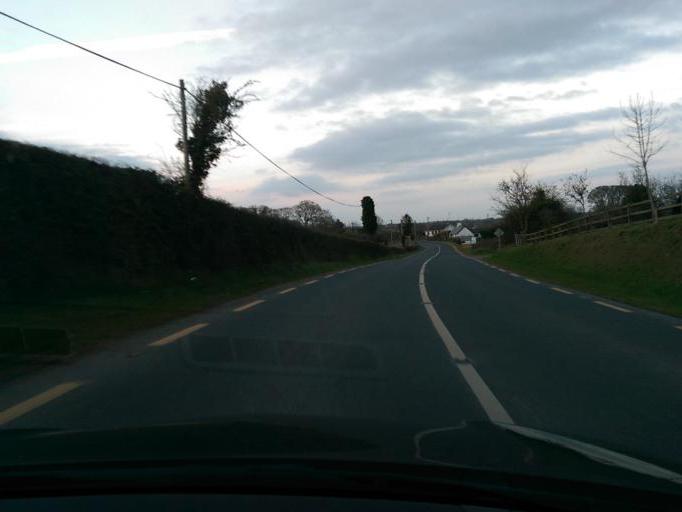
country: IE
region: Connaught
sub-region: County Galway
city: Portumna
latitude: 53.0026
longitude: -8.1261
